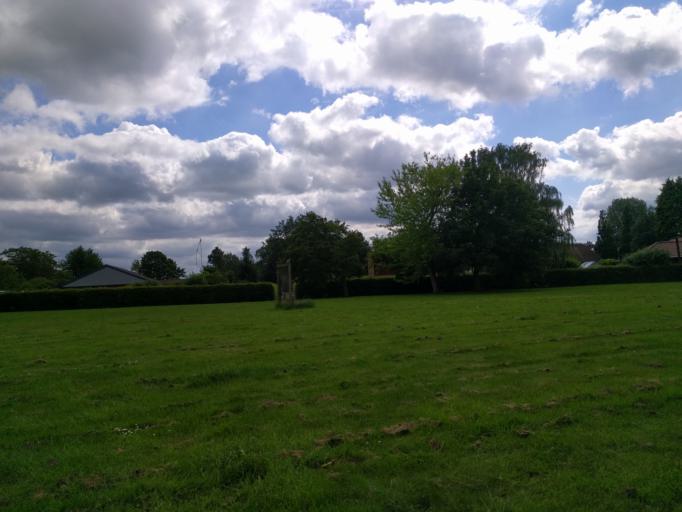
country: DK
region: South Denmark
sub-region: Kerteminde Kommune
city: Munkebo
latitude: 55.4478
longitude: 10.5508
